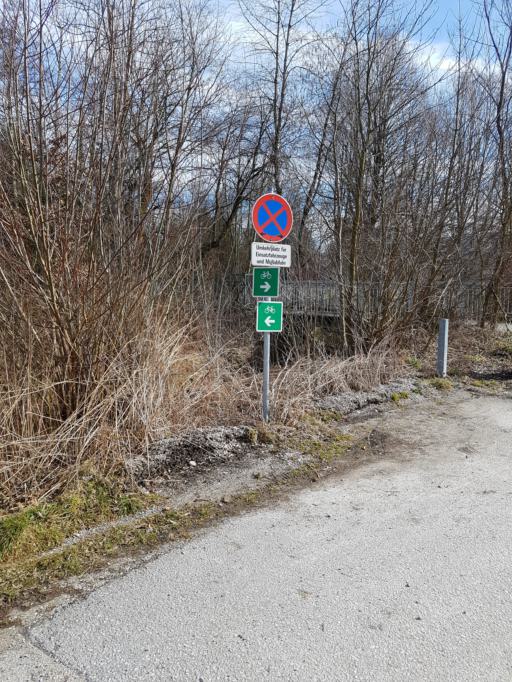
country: AT
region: Salzburg
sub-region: Politischer Bezirk Salzburg-Umgebung
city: Henndorf am Wallersee
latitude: 47.9197
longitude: 13.1644
